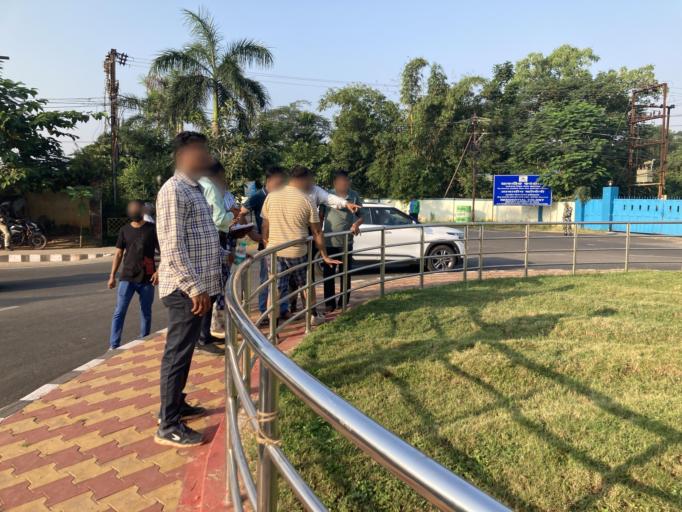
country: IN
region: Odisha
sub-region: Khordha
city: Bhubaneshwar
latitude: 20.2523
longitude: 85.8248
